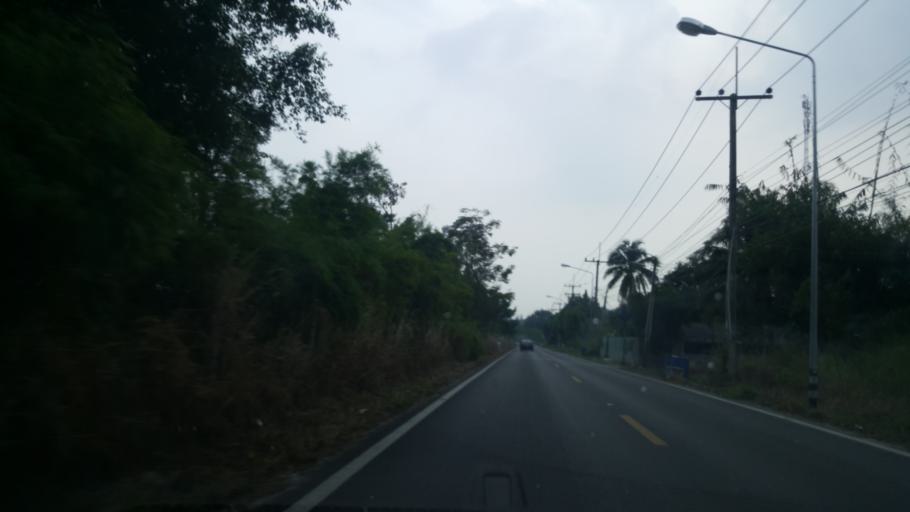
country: TH
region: Chon Buri
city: Ban Bueng
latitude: 13.2153
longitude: 101.0487
